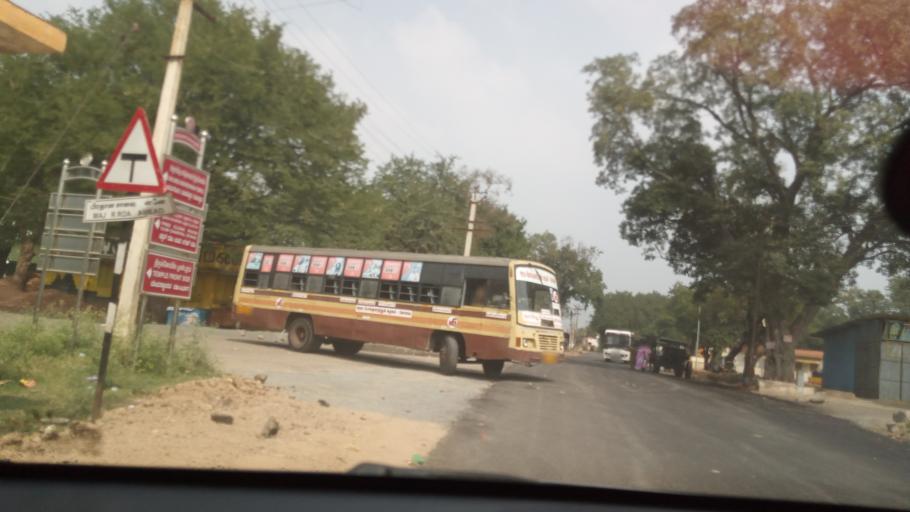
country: IN
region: Tamil Nadu
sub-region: Erode
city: Sathyamangalam
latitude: 11.5523
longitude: 77.1385
